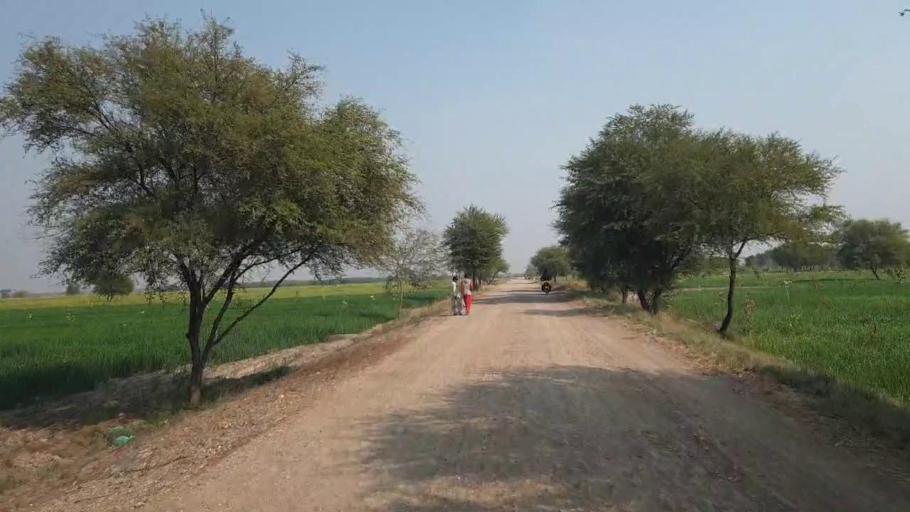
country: PK
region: Sindh
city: Mirwah Gorchani
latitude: 25.3506
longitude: 68.9398
